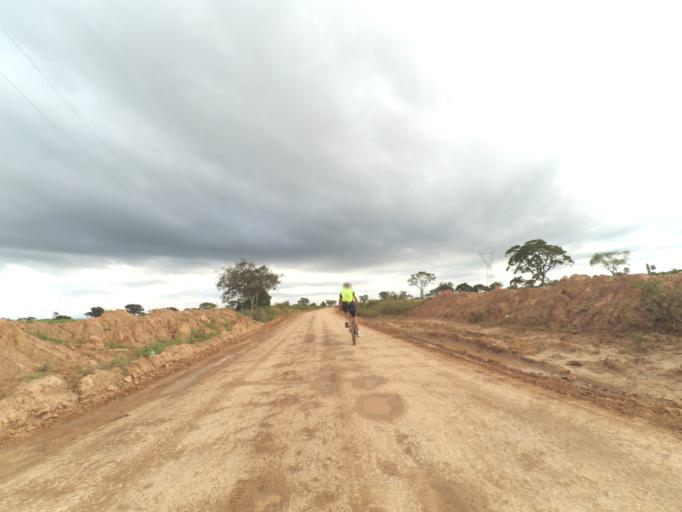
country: BO
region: Santa Cruz
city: Santa Cruz de la Sierra
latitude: -17.7129
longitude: -63.2772
